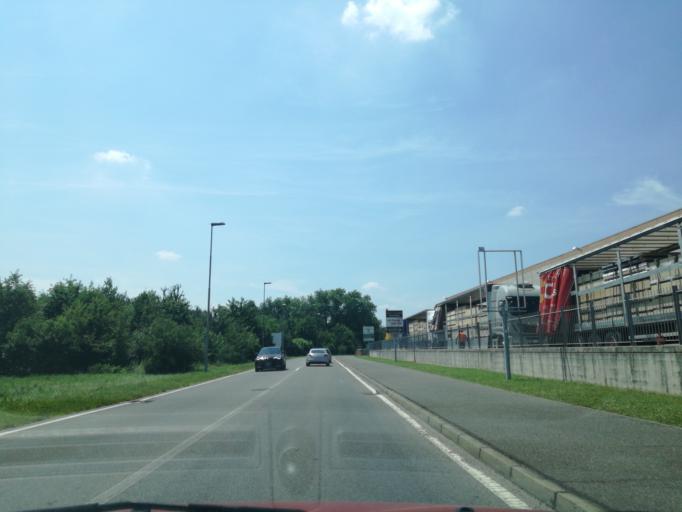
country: IT
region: Lombardy
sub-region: Provincia di Monza e Brianza
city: Biassono
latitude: 45.6276
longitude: 9.2537
